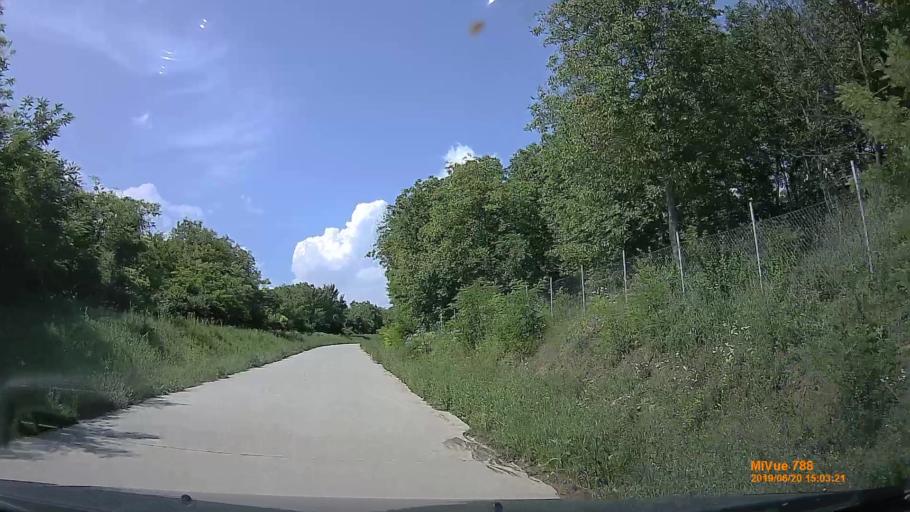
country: HU
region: Baranya
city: Kozarmisleny
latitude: 45.9872
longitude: 18.2620
